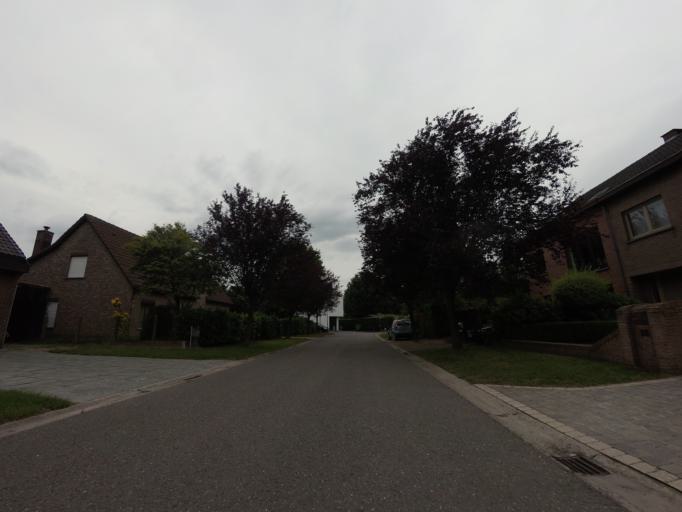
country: BE
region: Flanders
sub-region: Provincie Antwerpen
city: Schilde
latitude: 51.2405
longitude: 4.5915
